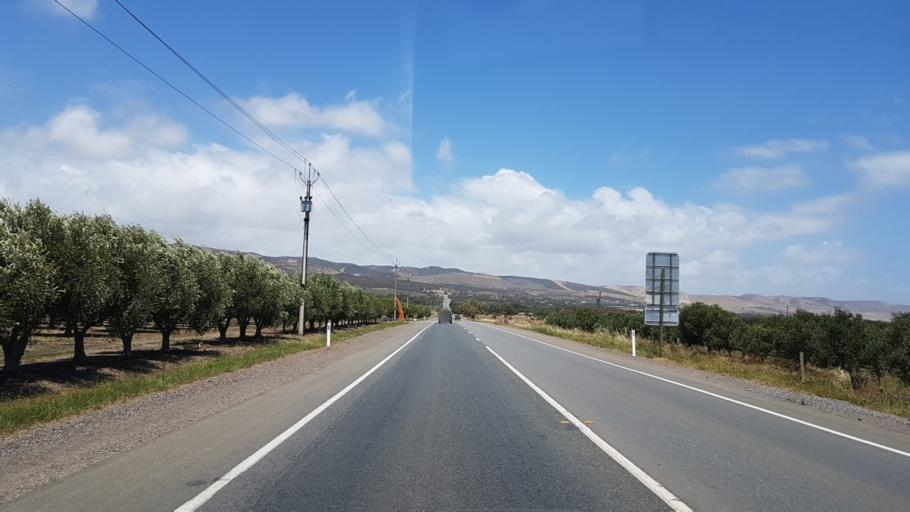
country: AU
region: South Australia
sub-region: Onkaparinga
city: Aldinga
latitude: -35.2985
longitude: 138.4726
